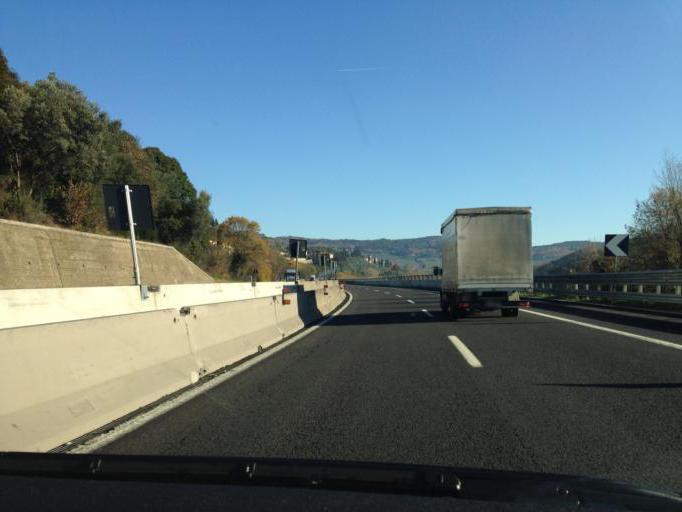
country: IT
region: Tuscany
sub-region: Province of Florence
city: Antella
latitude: 43.7277
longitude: 11.3473
